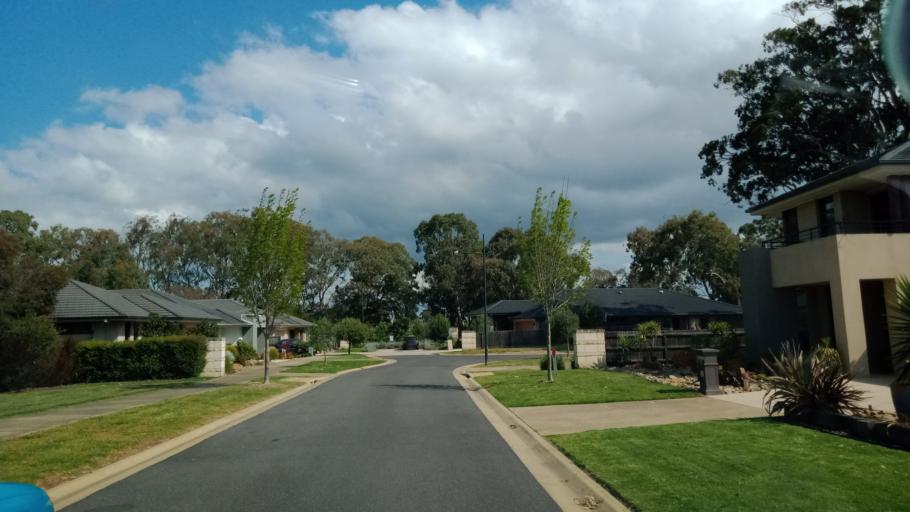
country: AU
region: Victoria
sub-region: Frankston
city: Sandhurst
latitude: -38.0881
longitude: 145.2081
